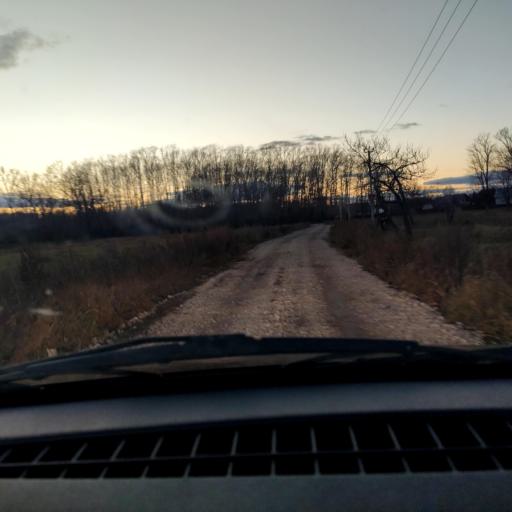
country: RU
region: Bashkortostan
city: Ufa
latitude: 54.6470
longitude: 55.9020
